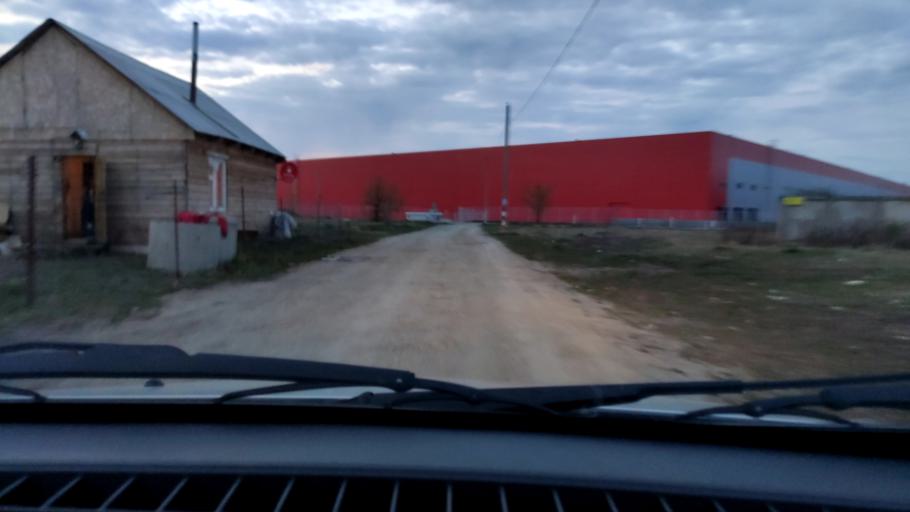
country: RU
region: Voronezj
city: Podgornoye
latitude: 51.7990
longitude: 39.2150
